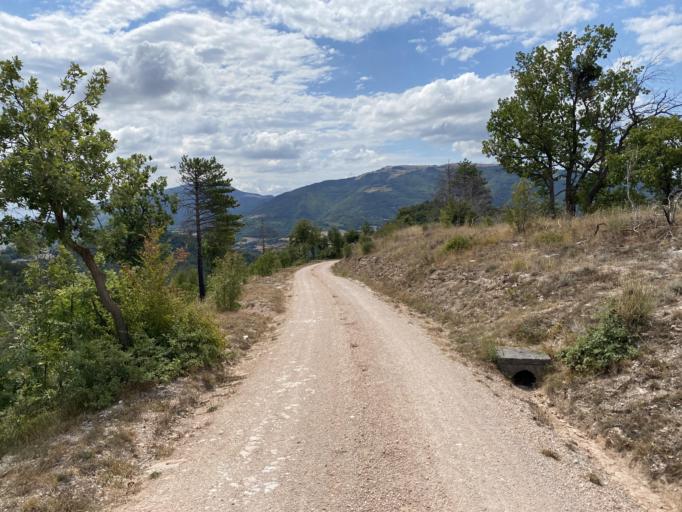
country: IT
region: The Marches
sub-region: Provincia di Pesaro e Urbino
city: Canavaccio
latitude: 43.7086
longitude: 12.7149
